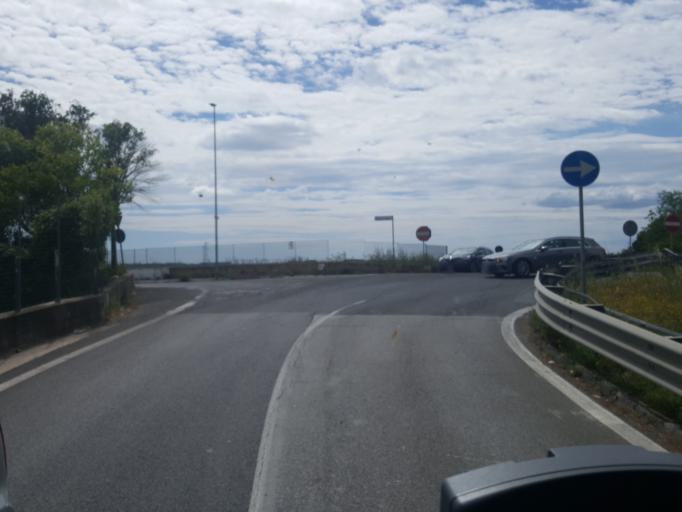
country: IT
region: Latium
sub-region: Citta metropolitana di Roma Capitale
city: La Massimina-Casal Lumbroso
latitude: 41.8818
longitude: 12.3472
